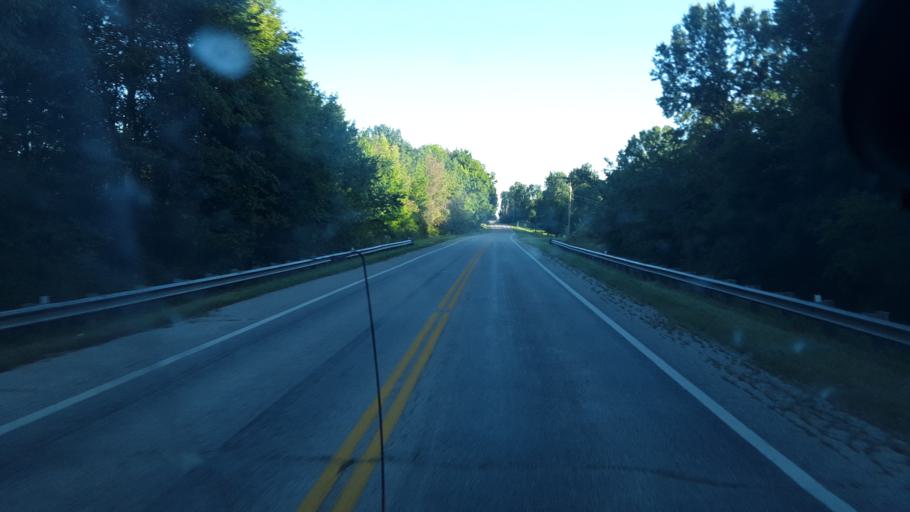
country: US
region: Ohio
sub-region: Mahoning County
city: Craig Beach
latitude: 41.1413
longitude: -81.0511
